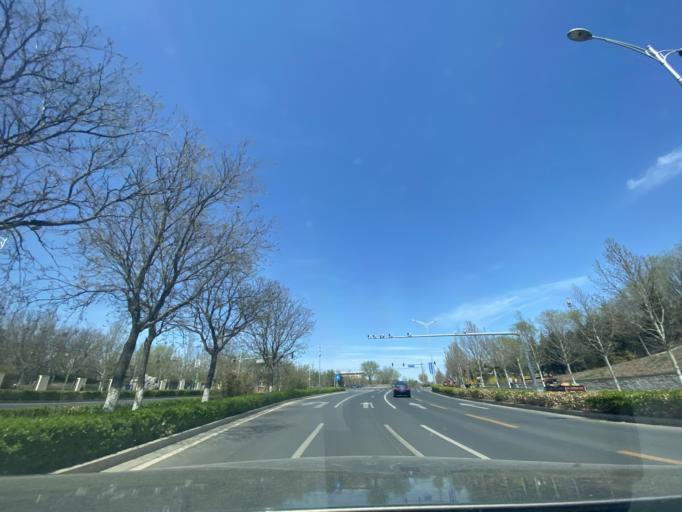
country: CN
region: Beijing
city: Sijiqing
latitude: 39.9383
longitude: 116.2404
